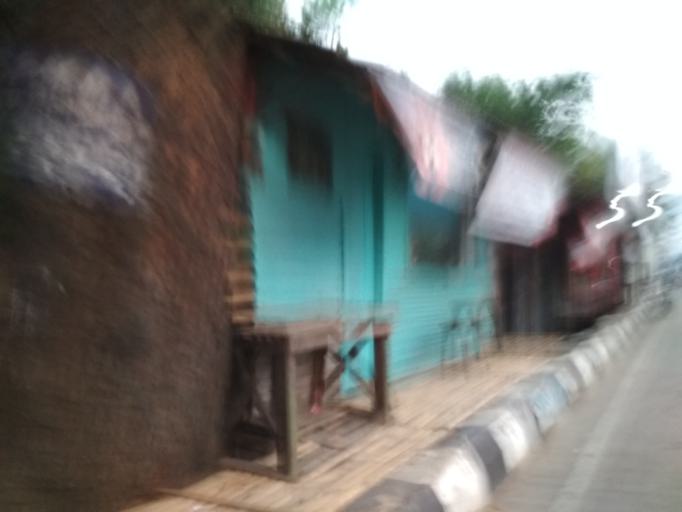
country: ID
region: West Java
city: Caringin
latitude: -6.6718
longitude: 106.8470
